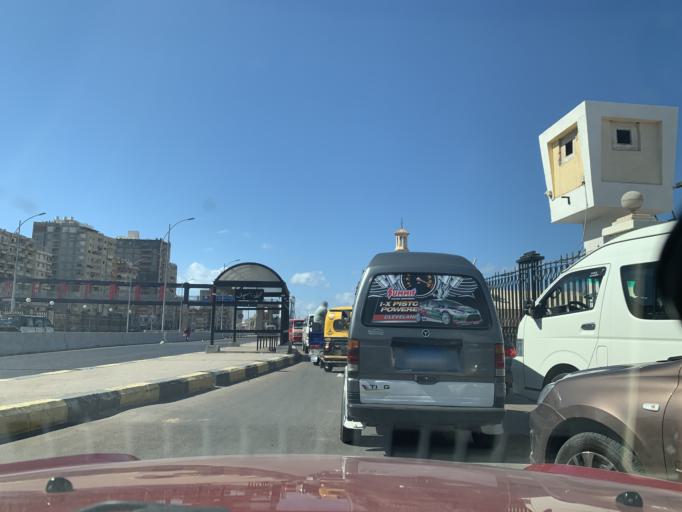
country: EG
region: Alexandria
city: Alexandria
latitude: 31.2202
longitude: 29.9914
